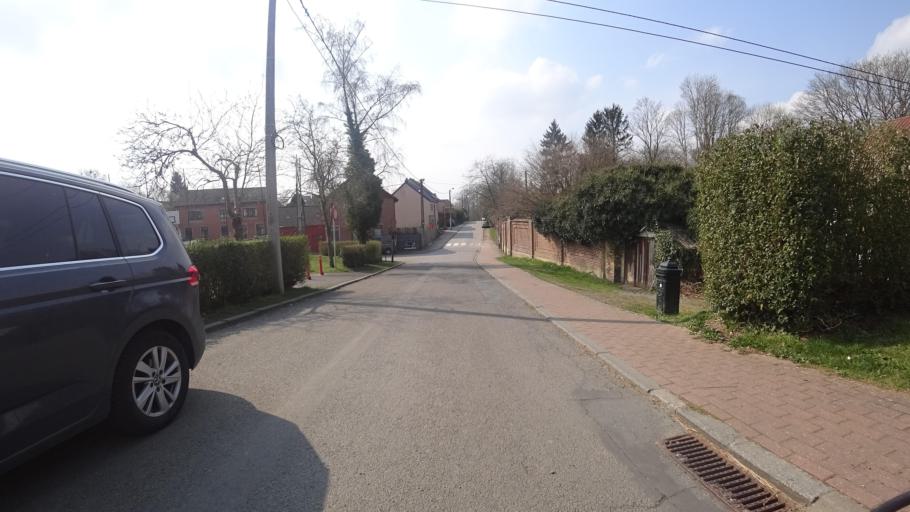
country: BE
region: Wallonia
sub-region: Province du Brabant Wallon
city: Chastre-Villeroux-Blanmont
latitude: 50.6235
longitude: 4.6421
